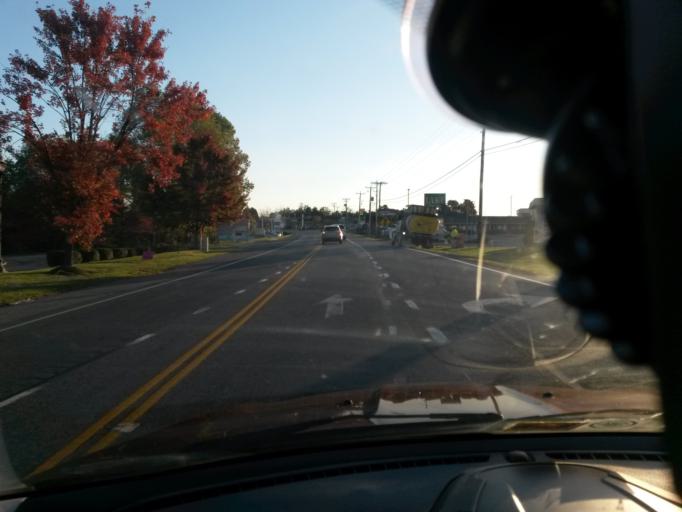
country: US
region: Virginia
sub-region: Franklin County
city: North Shore
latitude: 37.1195
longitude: -79.7159
